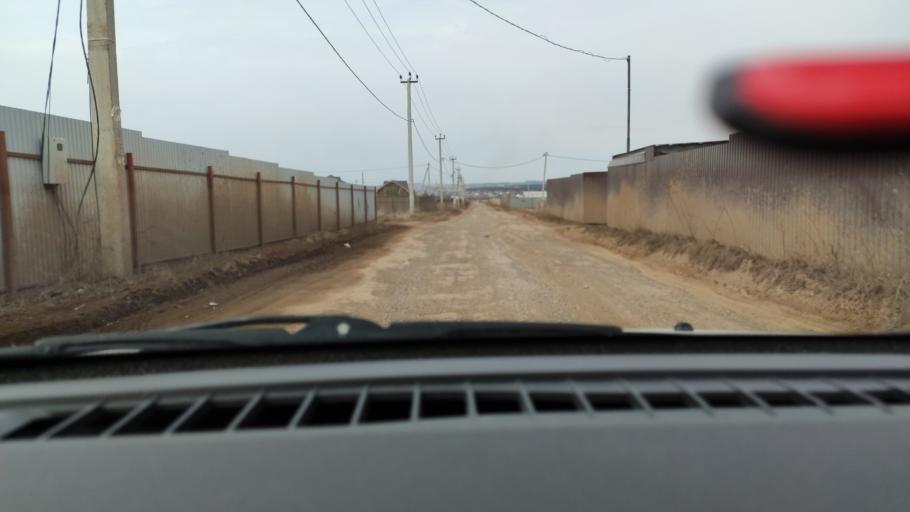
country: RU
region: Perm
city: Kultayevo
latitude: 57.8988
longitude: 56.0006
